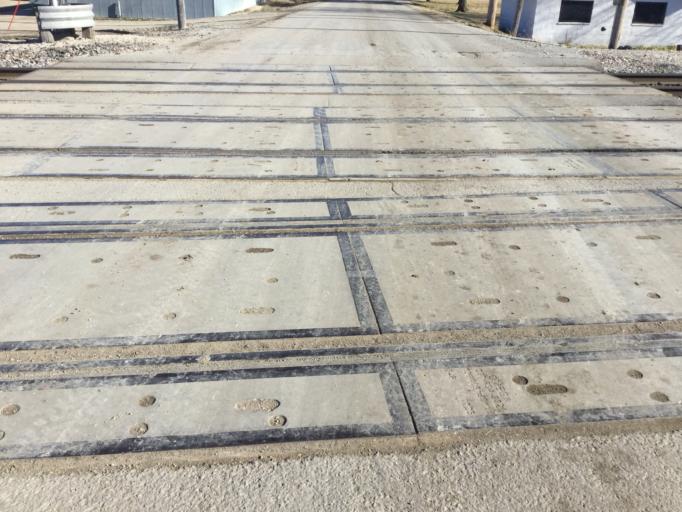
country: US
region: Kansas
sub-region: Bourbon County
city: Fort Scott
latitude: 37.9358
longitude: -94.6957
